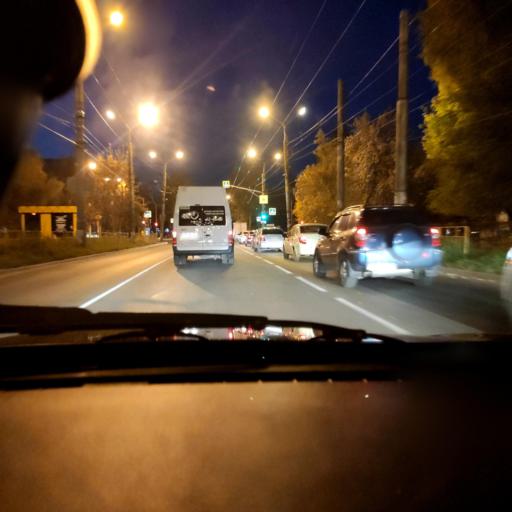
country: RU
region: Samara
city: Tol'yatti
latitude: 53.5297
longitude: 49.4124
